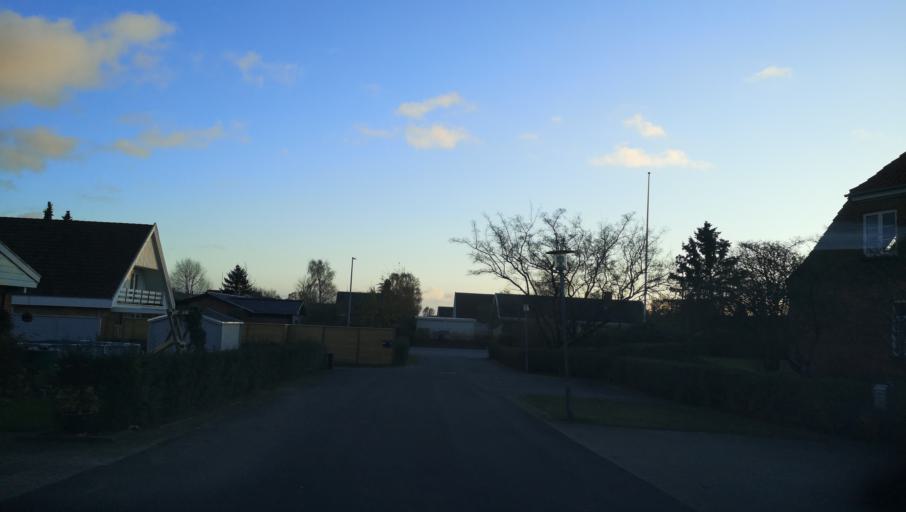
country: DK
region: Zealand
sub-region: Naestved Kommune
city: Naestved
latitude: 55.2287
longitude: 11.7338
